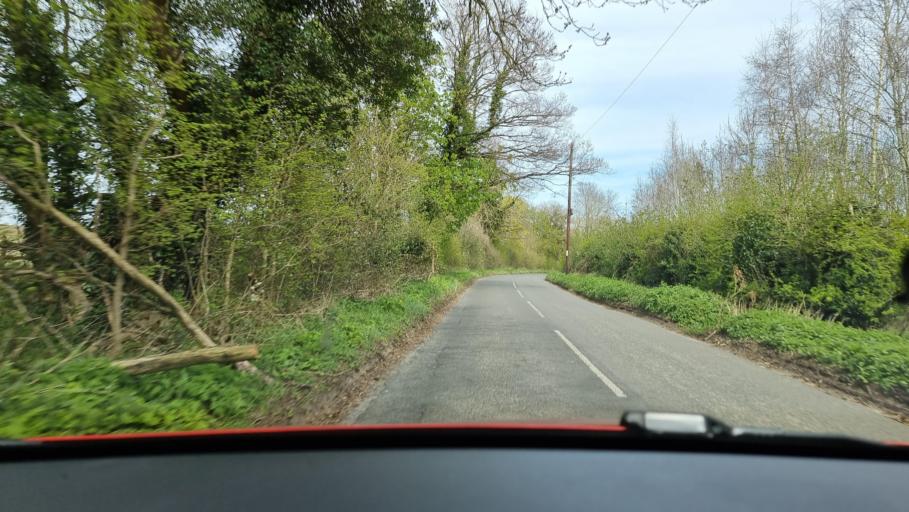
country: GB
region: England
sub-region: Oxfordshire
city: Oxford
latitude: 51.8064
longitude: -1.2224
